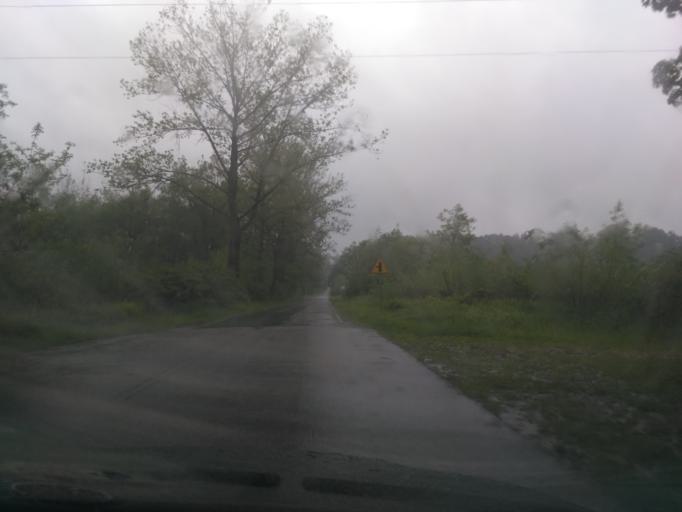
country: PL
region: Subcarpathian Voivodeship
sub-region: Powiat jasielski
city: Debowiec
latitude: 49.6818
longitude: 21.4722
